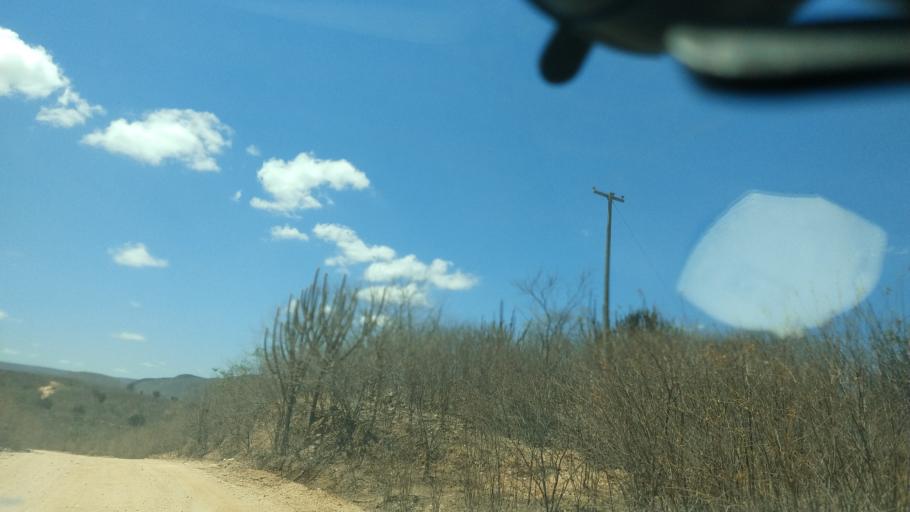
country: BR
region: Rio Grande do Norte
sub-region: Cerro Cora
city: Cerro Cora
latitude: -6.0111
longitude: -36.3012
